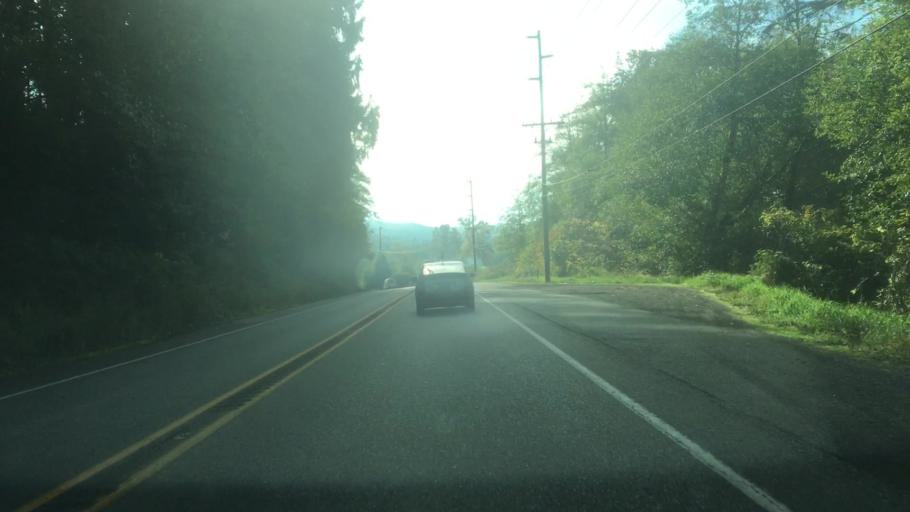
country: US
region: Washington
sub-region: Grays Harbor County
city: Montesano
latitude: 46.9544
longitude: -123.6102
